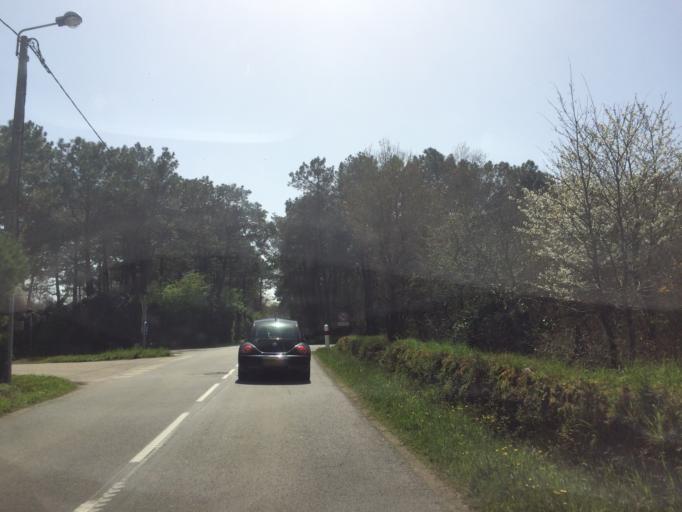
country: FR
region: Brittany
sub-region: Departement du Morbihan
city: Ploemel
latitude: 47.6274
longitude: -3.0497
